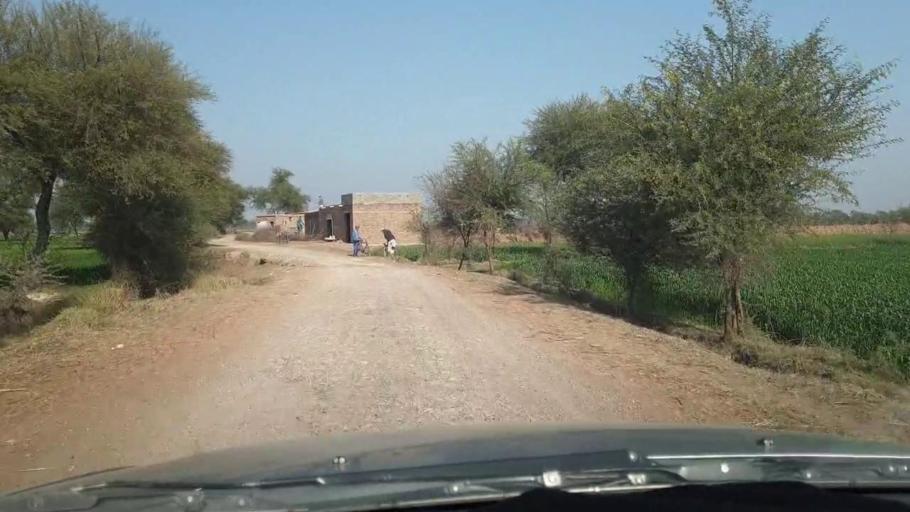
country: PK
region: Sindh
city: Mirpur Mathelo
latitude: 27.9281
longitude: 69.5620
